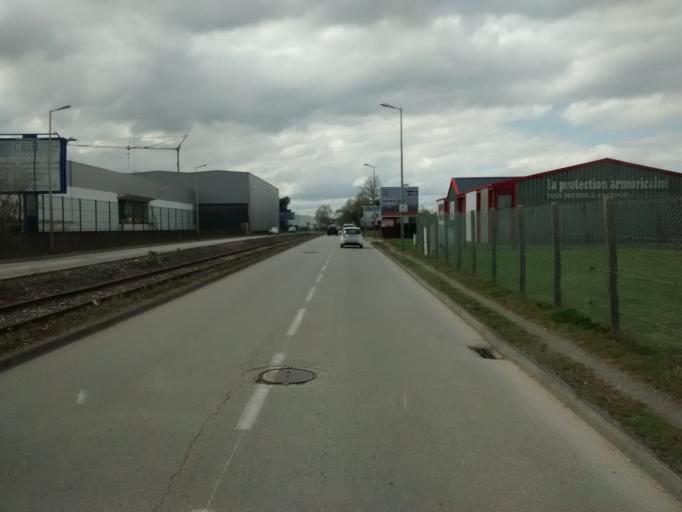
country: FR
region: Brittany
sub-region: Departement du Morbihan
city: Vannes
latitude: 47.6621
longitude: -2.7225
